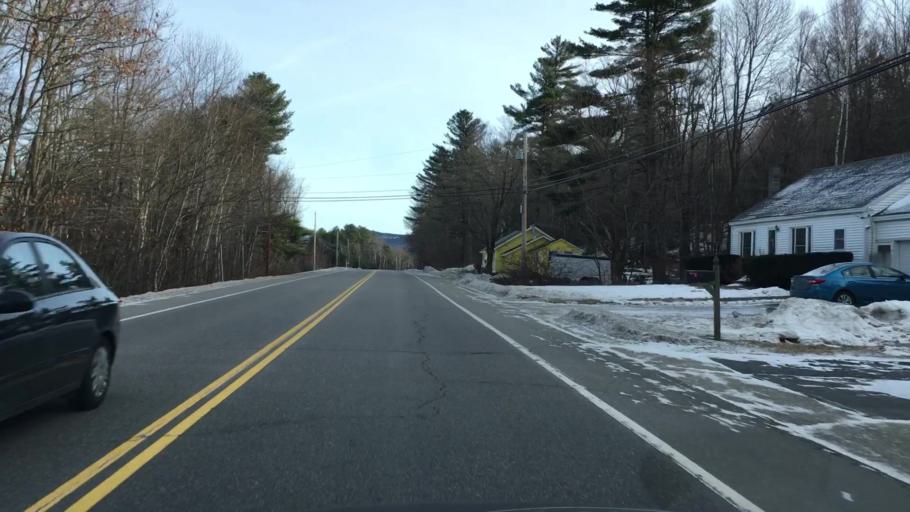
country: US
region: New Hampshire
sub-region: Sullivan County
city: Sunapee
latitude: 43.3443
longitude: -72.0921
